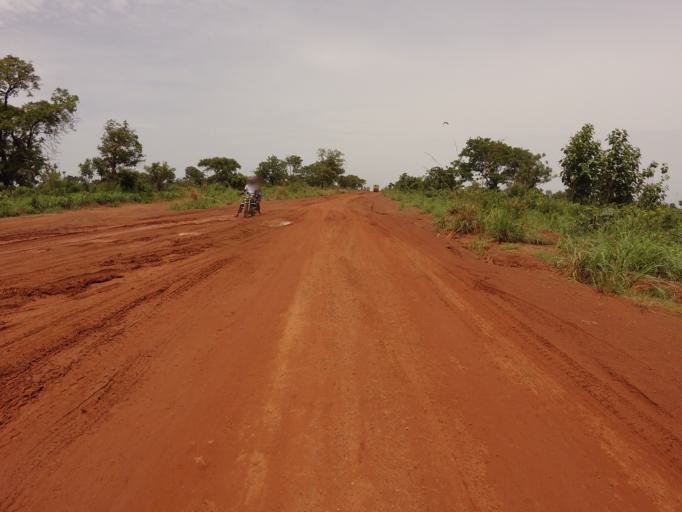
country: GH
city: Kpandae
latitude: 8.7864
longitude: 0.0574
